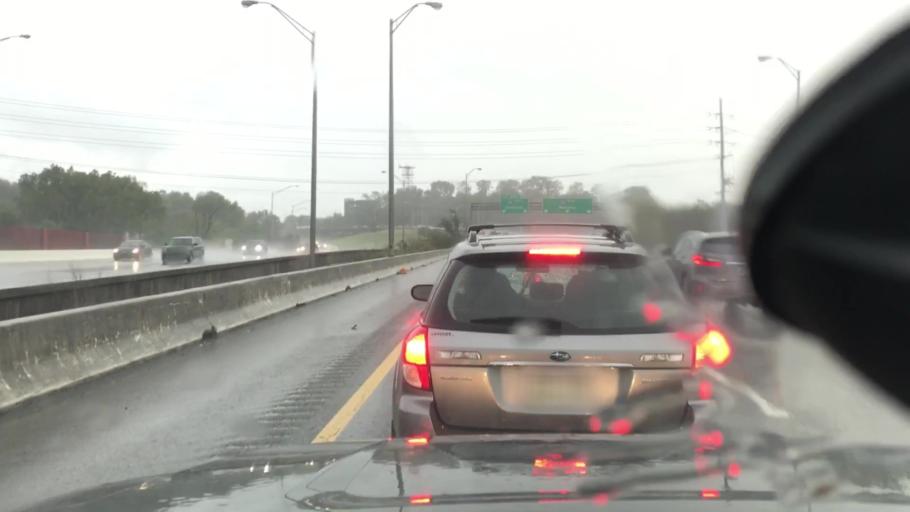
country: US
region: Tennessee
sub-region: Davidson County
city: Nashville
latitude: 36.1630
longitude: -86.8215
